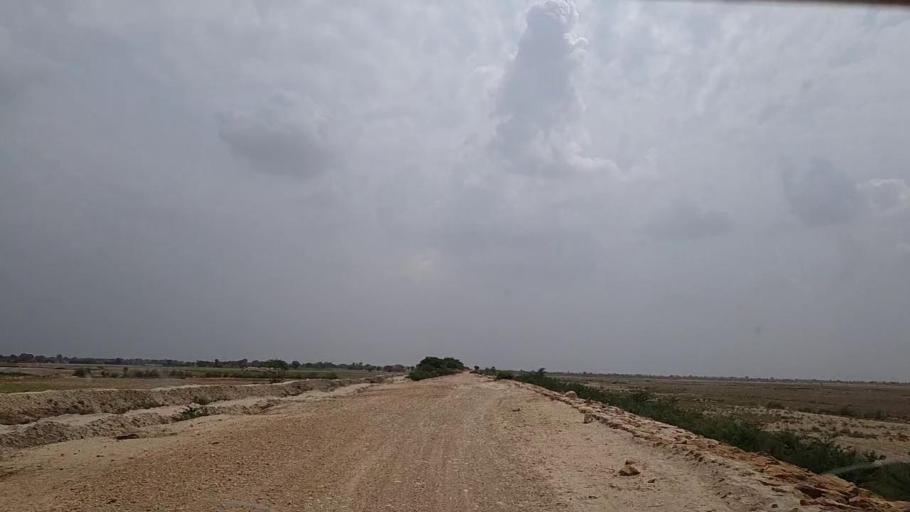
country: PK
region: Sindh
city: Johi
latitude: 26.7423
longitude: 67.5858
